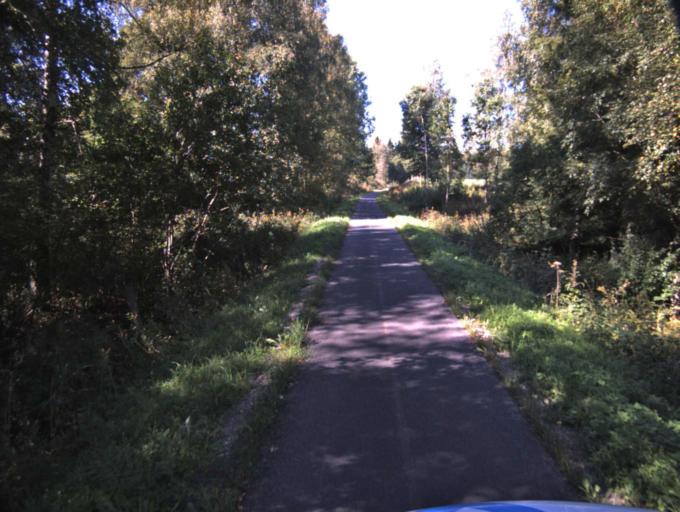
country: SE
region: Vaestra Goetaland
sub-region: Ulricehamns Kommun
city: Ulricehamn
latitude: 57.8044
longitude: 13.3620
